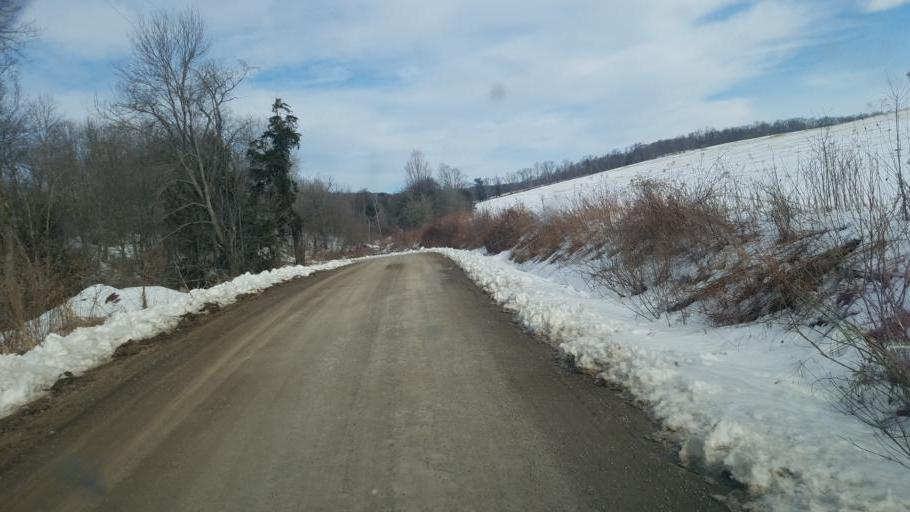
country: US
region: New York
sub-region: Allegany County
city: Andover
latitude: 41.9571
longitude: -77.7794
